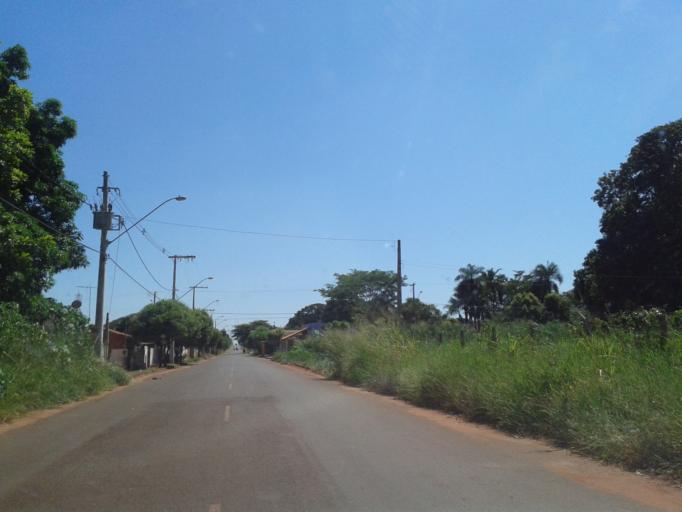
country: BR
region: Minas Gerais
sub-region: Ituiutaba
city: Ituiutaba
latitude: -19.0013
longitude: -49.4542
